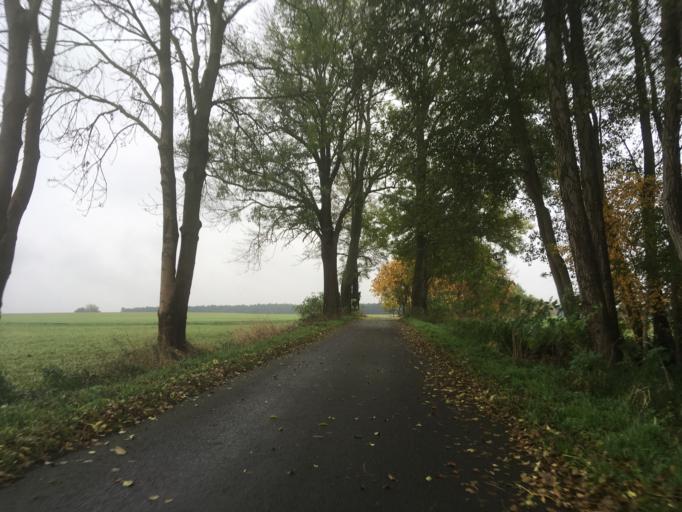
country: DE
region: Brandenburg
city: Neu Zauche
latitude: 52.0275
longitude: 14.1167
